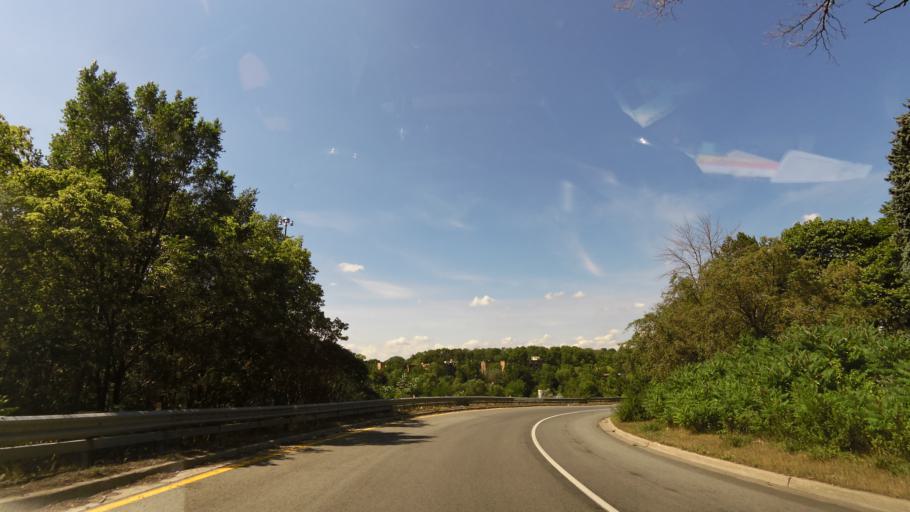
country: CA
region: Ontario
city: Hamilton
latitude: 43.2622
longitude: -79.8922
